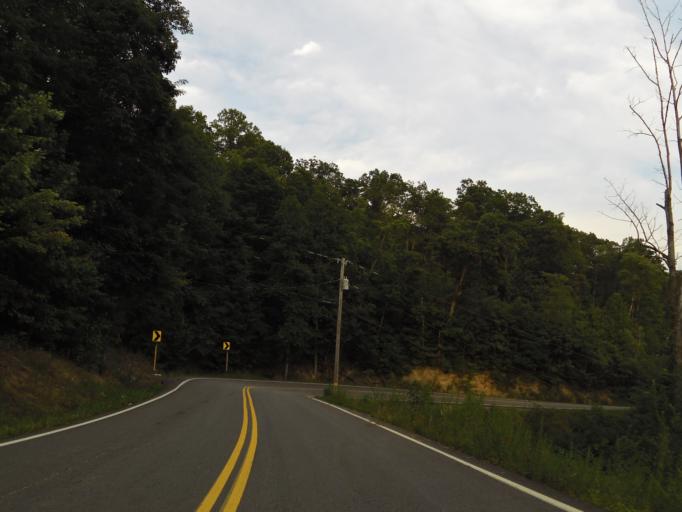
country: US
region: Tennessee
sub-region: Anderson County
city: Clinton
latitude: 36.1338
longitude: -84.2351
